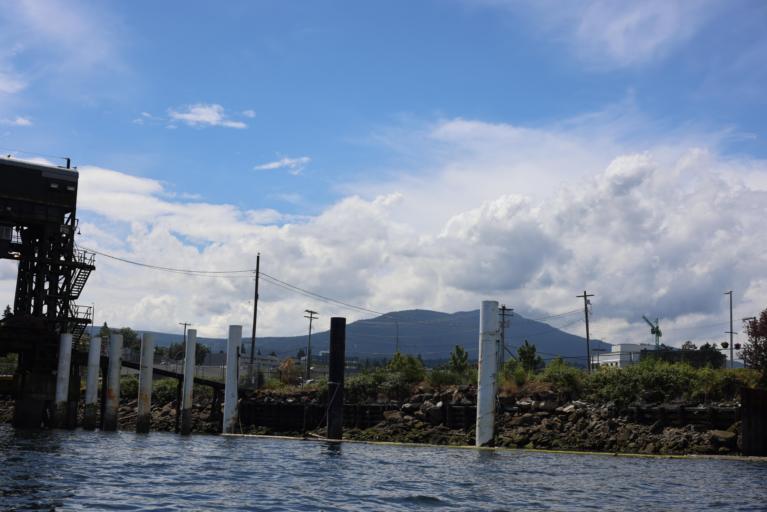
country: CA
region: British Columbia
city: Nanaimo
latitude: 49.1660
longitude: -123.9294
